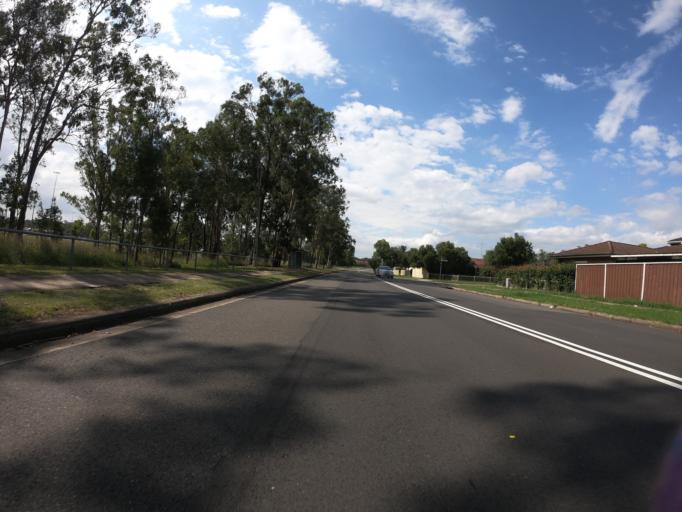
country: AU
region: New South Wales
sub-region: Blacktown
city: Hassall Grove
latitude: -33.7388
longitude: 150.8359
